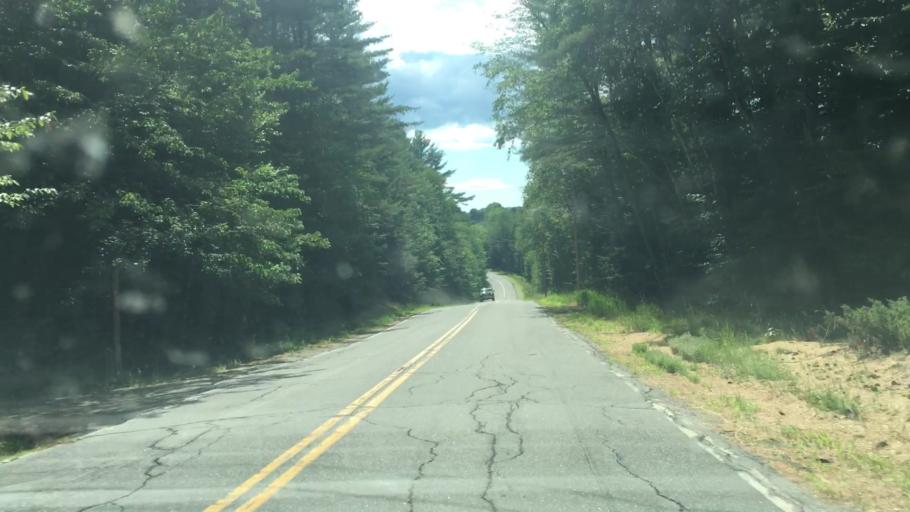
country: US
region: Maine
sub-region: Franklin County
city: Farmington
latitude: 44.7073
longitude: -70.0952
